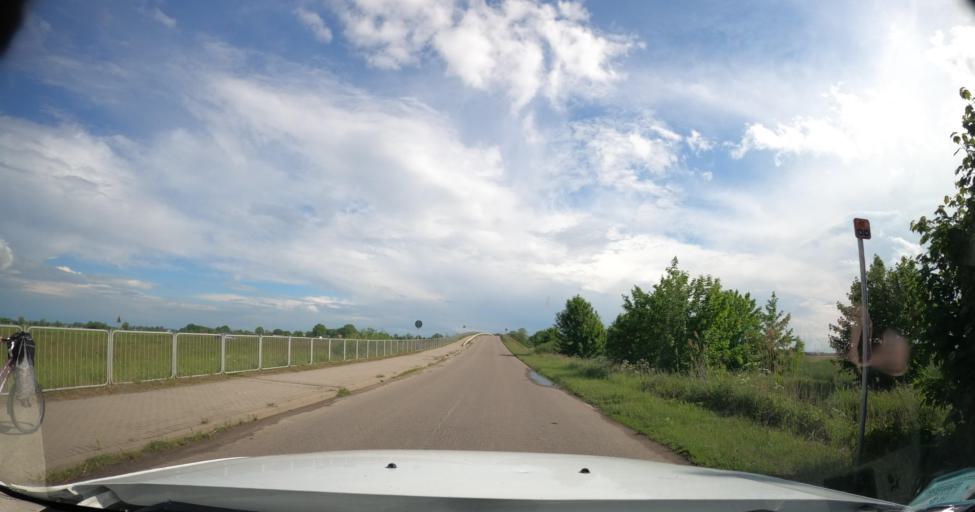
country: PL
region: Pomeranian Voivodeship
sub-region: Powiat nowodworski
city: Nowy Dwor Gdanski
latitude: 54.1963
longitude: 19.1400
